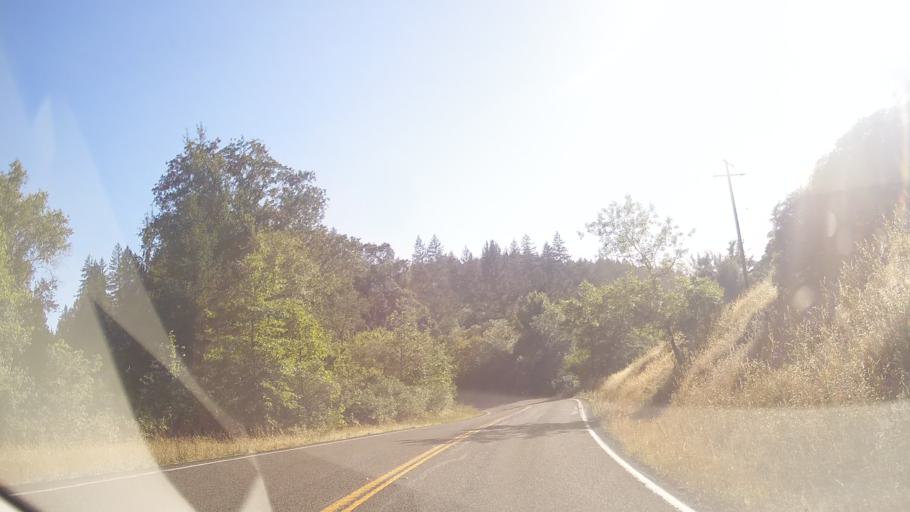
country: US
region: California
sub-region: Mendocino County
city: Willits
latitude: 39.4031
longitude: -123.3887
